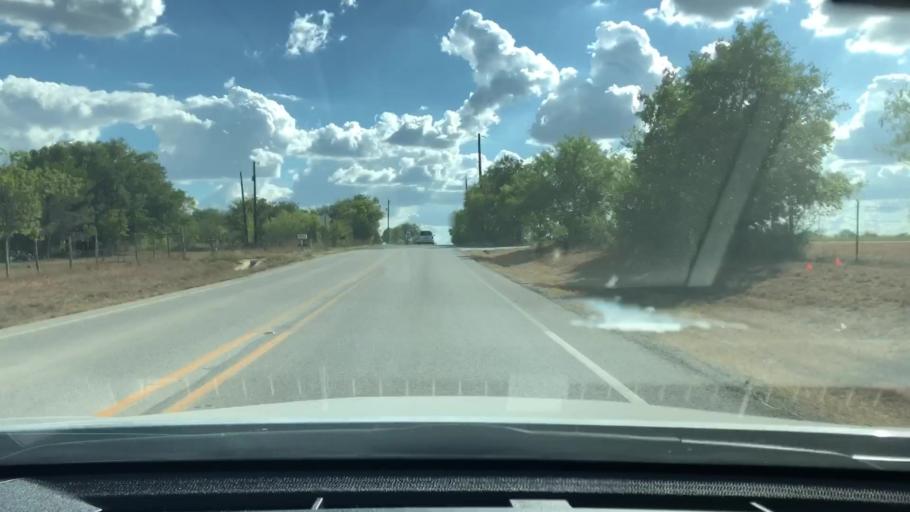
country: US
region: Texas
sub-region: Guadalupe County
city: Northcliff
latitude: 29.6311
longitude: -98.2456
